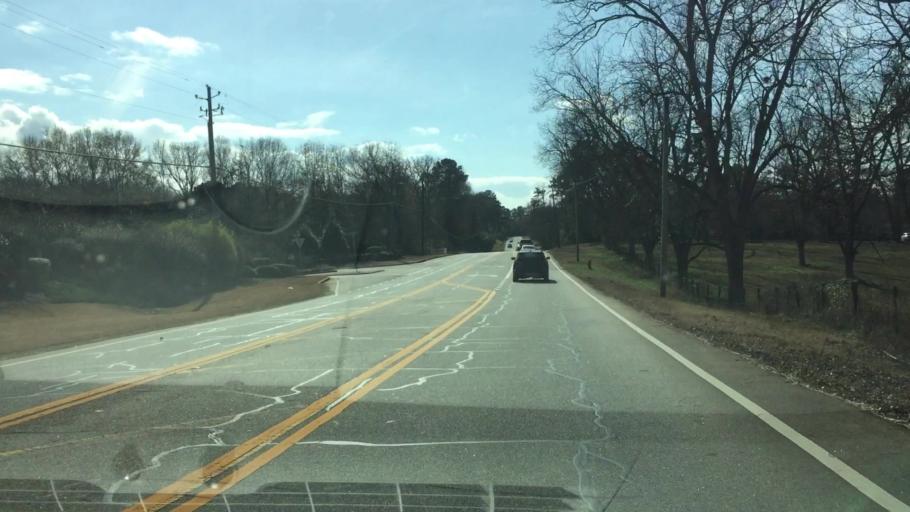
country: US
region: Georgia
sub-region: Henry County
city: McDonough
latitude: 33.4685
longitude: -84.1399
